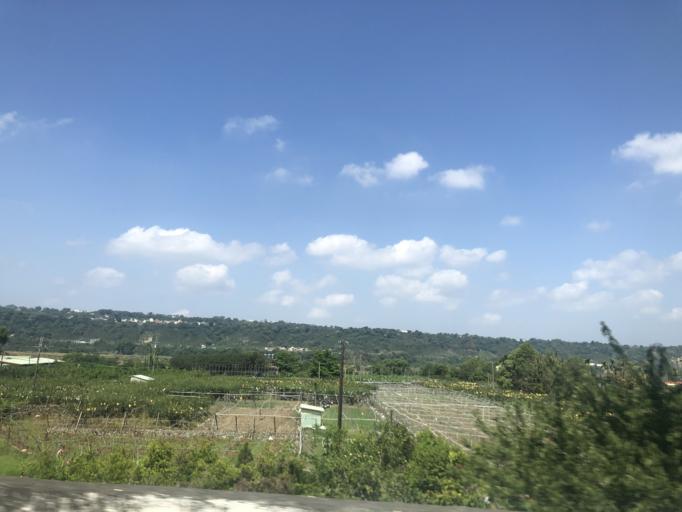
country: TW
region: Taiwan
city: Fengyuan
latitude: 24.2088
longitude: 120.8397
